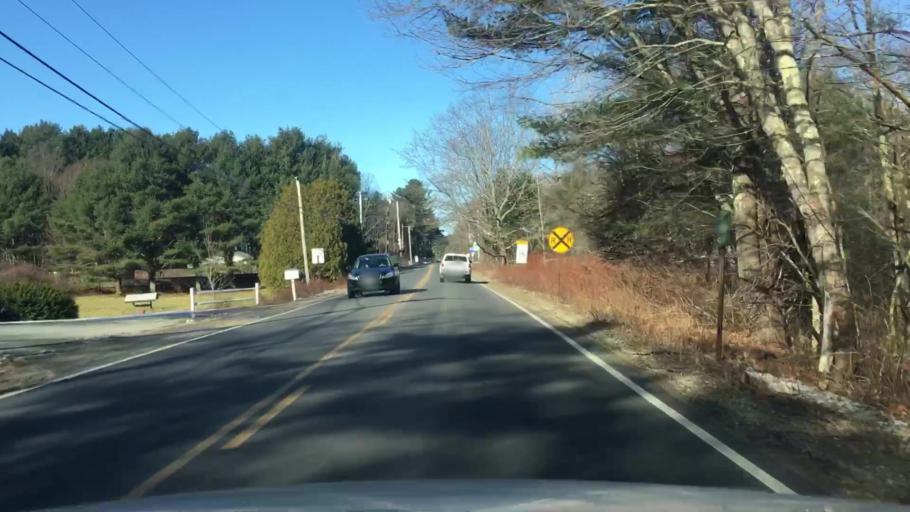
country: US
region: Maine
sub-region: York County
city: Arundel
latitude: 43.4145
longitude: -70.4996
